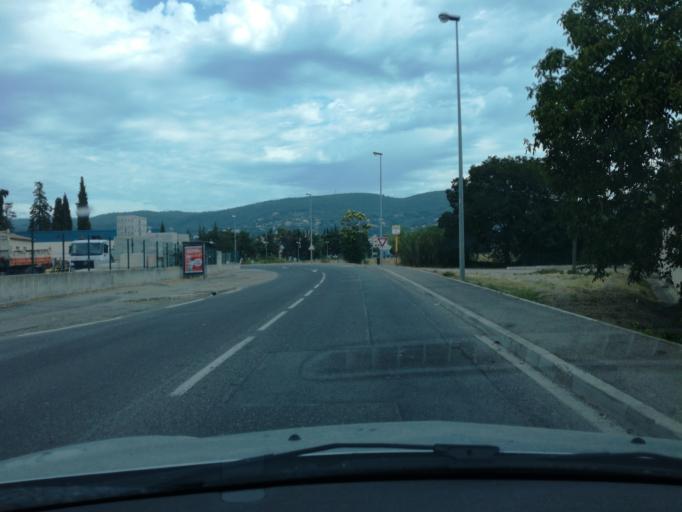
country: FR
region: Provence-Alpes-Cote d'Azur
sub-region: Departement du Var
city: Draguignan
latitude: 43.5302
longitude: 6.4496
